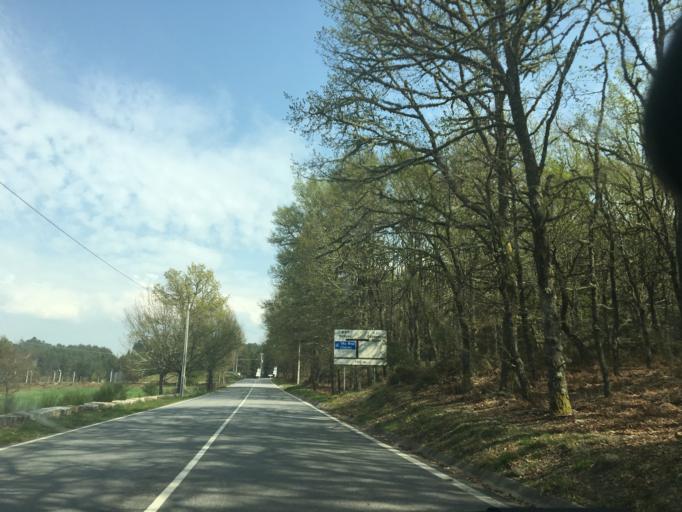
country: PT
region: Vila Real
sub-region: Boticas
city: Boticas
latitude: 41.6811
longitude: -7.7167
